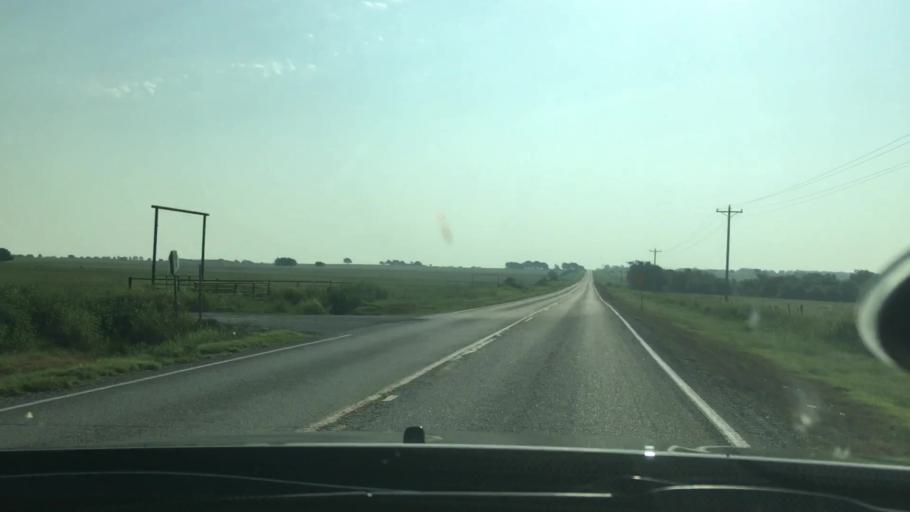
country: US
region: Oklahoma
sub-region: Bryan County
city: Durant
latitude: 34.1428
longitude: -96.3389
